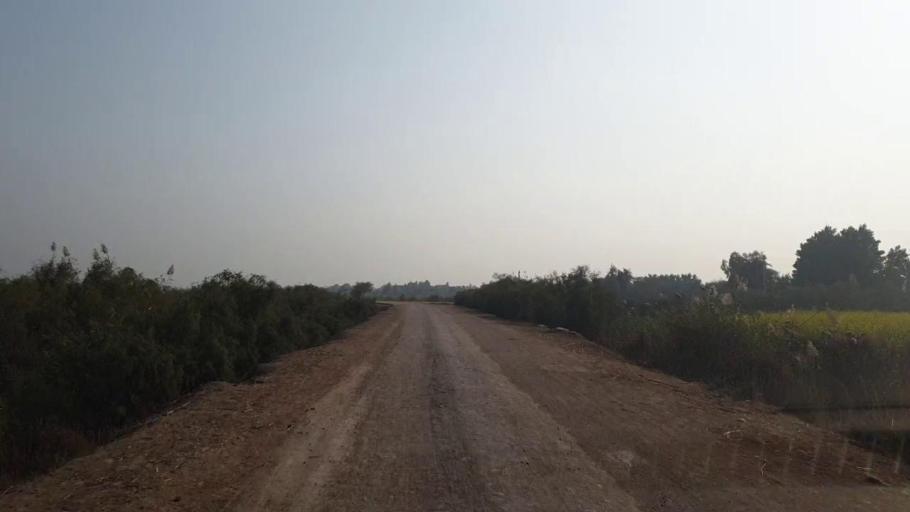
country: PK
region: Sindh
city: Shahdadpur
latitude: 25.9695
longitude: 68.5222
